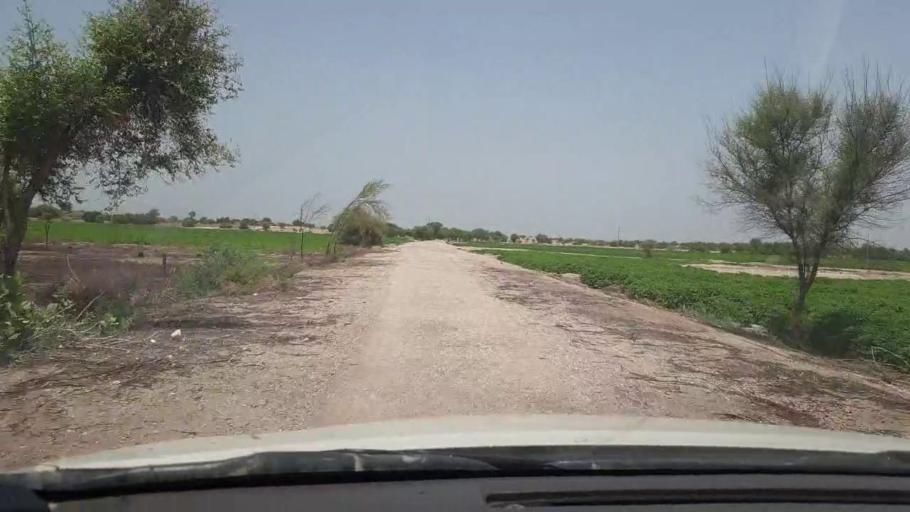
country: PK
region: Sindh
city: Rohri
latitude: 27.5123
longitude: 69.1845
